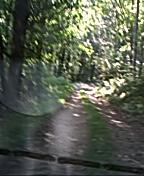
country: FR
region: Rhone-Alpes
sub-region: Departement de la Loire
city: La Pacaudiere
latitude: 46.1339
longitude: 3.7811
